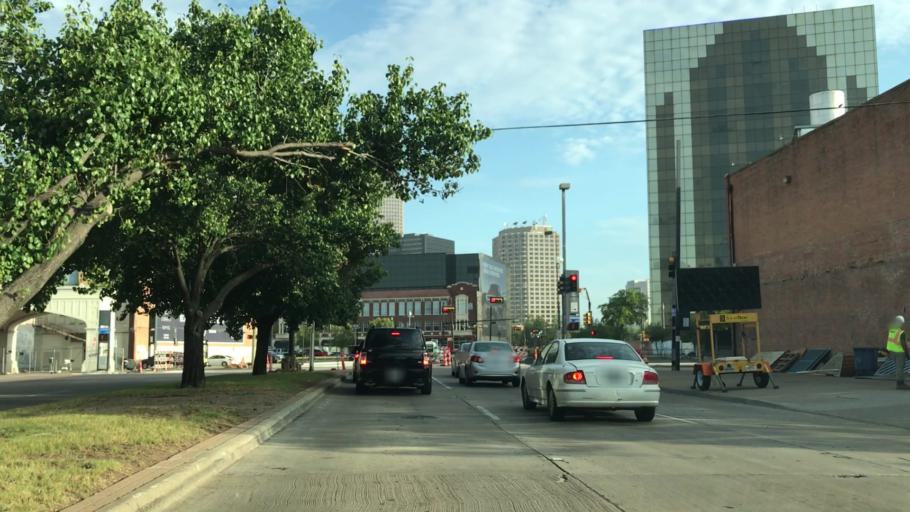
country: US
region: Texas
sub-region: Dallas County
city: Dallas
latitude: 32.7810
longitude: -96.7904
